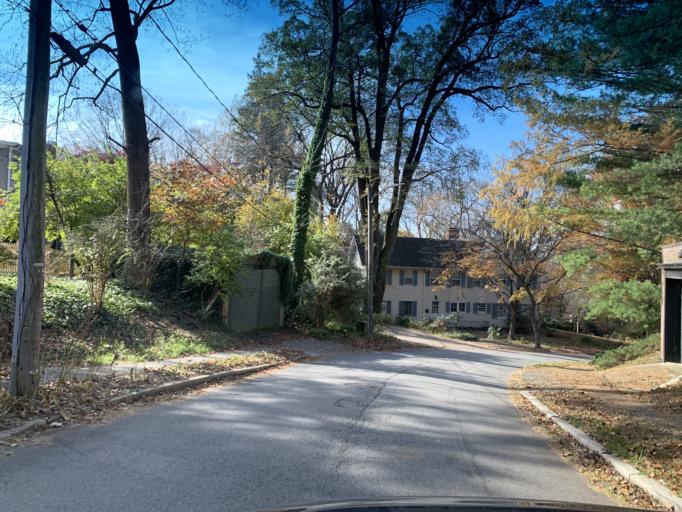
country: US
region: Maryland
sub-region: Baltimore County
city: Towson
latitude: 39.3560
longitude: -76.6391
